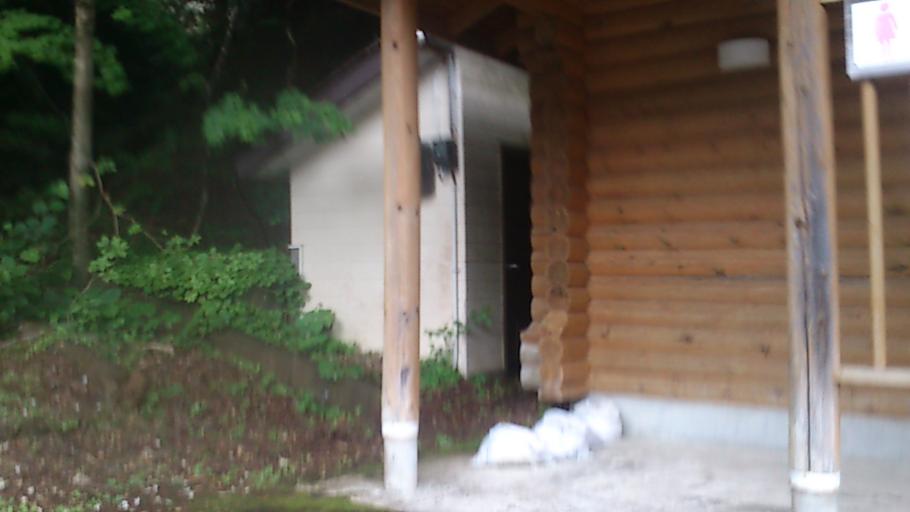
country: JP
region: Akita
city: Noshiromachi
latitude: 40.5594
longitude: 139.9623
